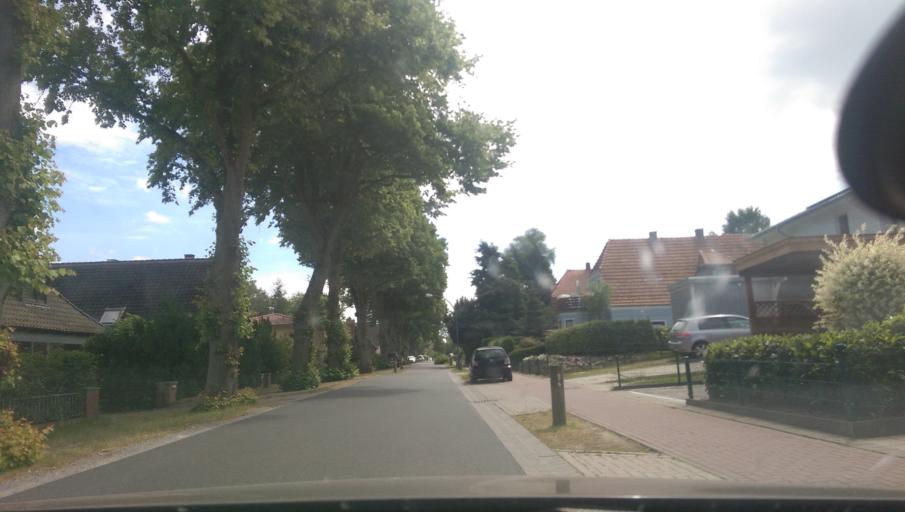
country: DE
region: Lower Saxony
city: Oyten
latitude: 53.0629
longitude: 9.0158
